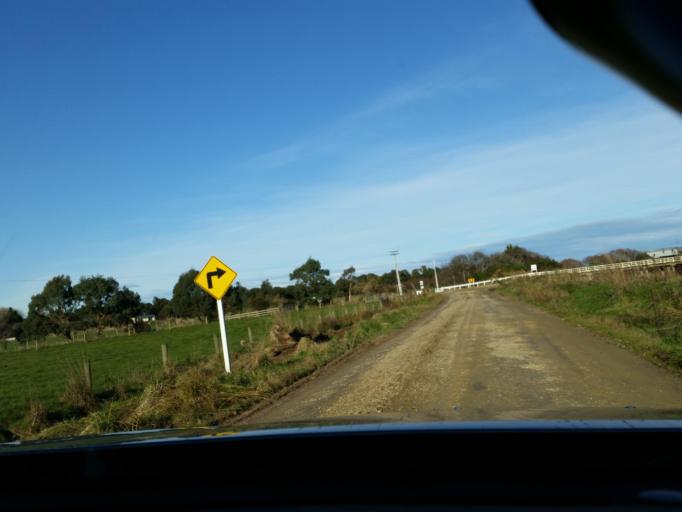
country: NZ
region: Southland
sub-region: Southland District
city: Winton
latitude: -46.2408
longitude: 168.4786
